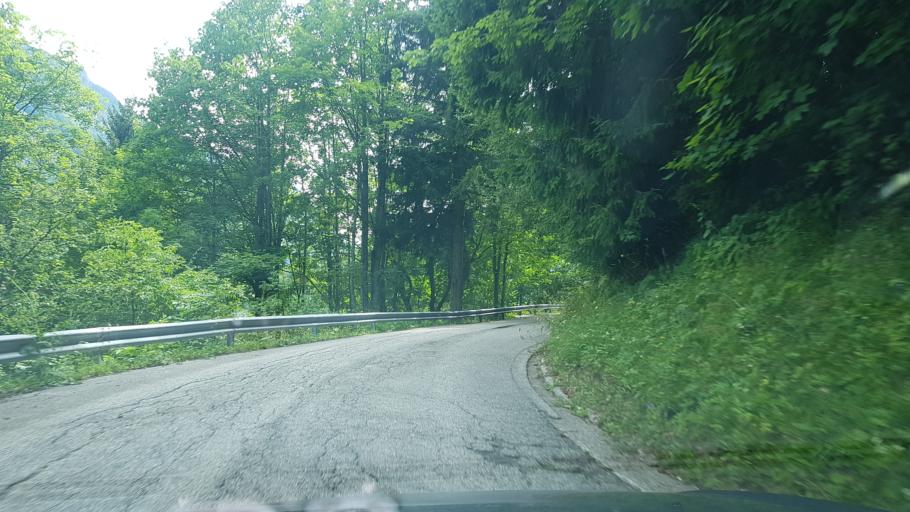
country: IT
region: Friuli Venezia Giulia
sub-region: Provincia di Udine
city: Pontebba
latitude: 46.5058
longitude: 13.2509
